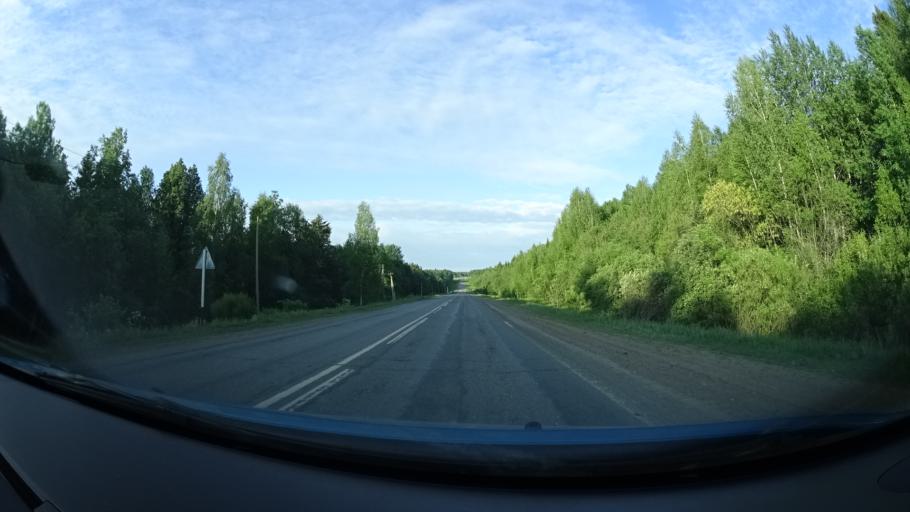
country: RU
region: Perm
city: Kultayevo
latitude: 57.8350
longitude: 55.8188
